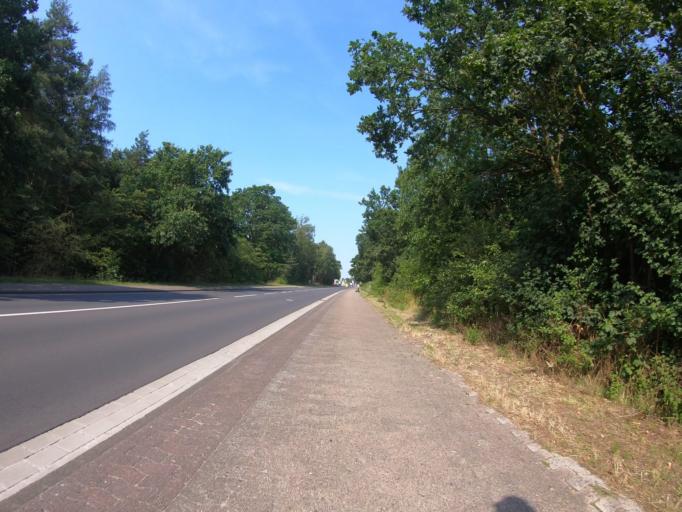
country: DE
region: Lower Saxony
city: Gifhorn
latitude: 52.4631
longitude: 10.5508
